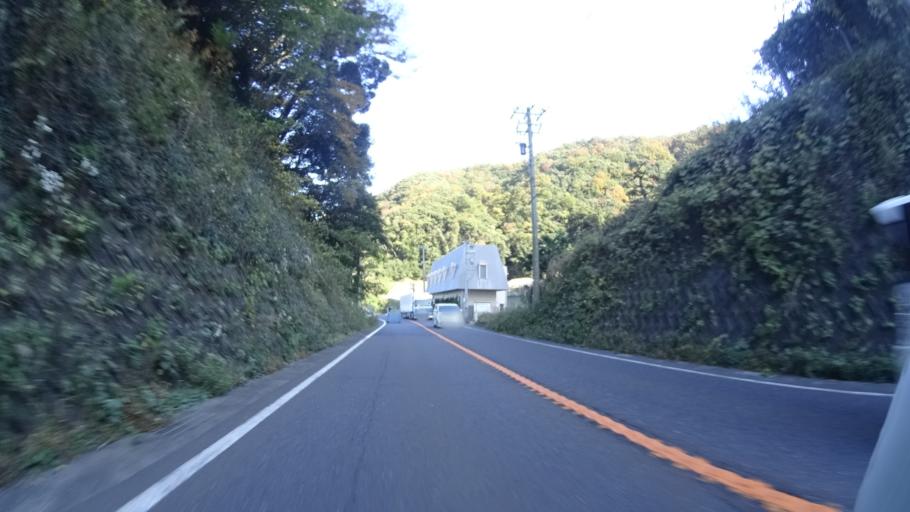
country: JP
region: Fukui
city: Tsuruga
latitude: 35.6925
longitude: 136.0817
